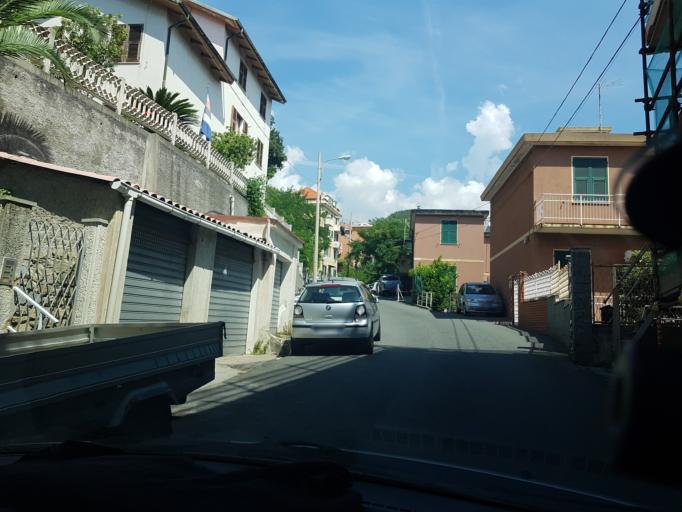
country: IT
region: Liguria
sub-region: Provincia di Genova
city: San Teodoro
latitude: 44.4327
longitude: 8.8418
